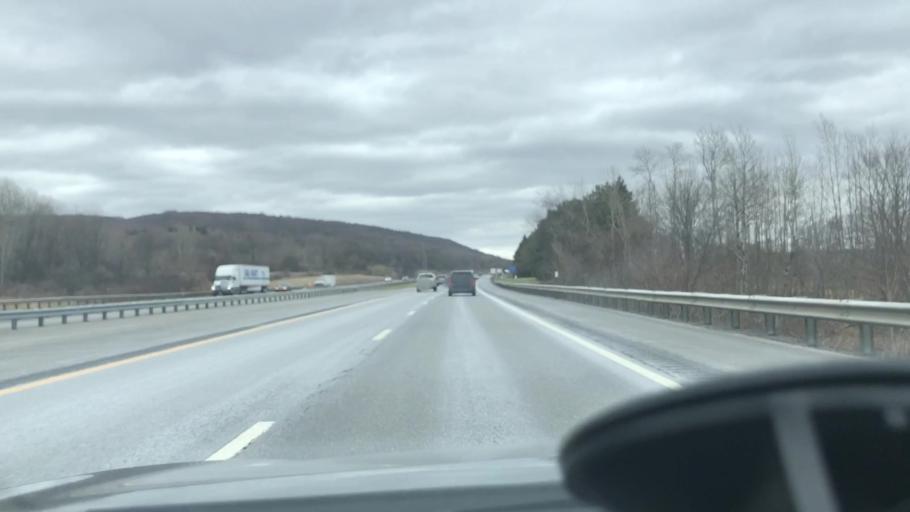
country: US
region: New York
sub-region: Herkimer County
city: Frankfort
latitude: 43.0550
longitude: -75.0668
